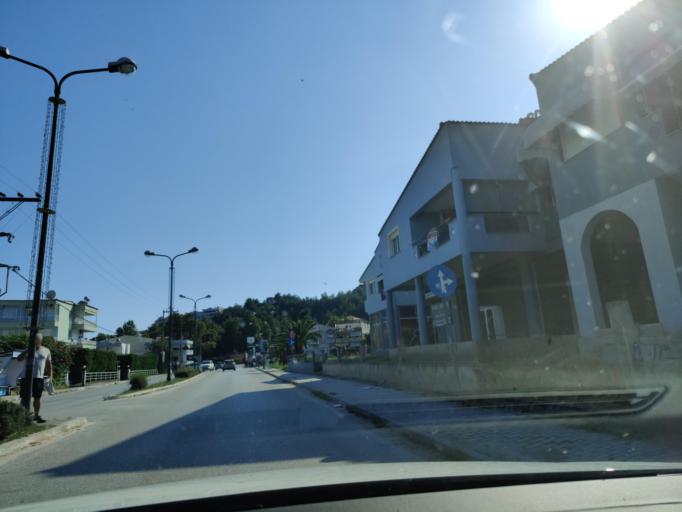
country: GR
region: East Macedonia and Thrace
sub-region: Nomos Kavalas
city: Nea Peramos
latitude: 40.8467
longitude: 24.3075
